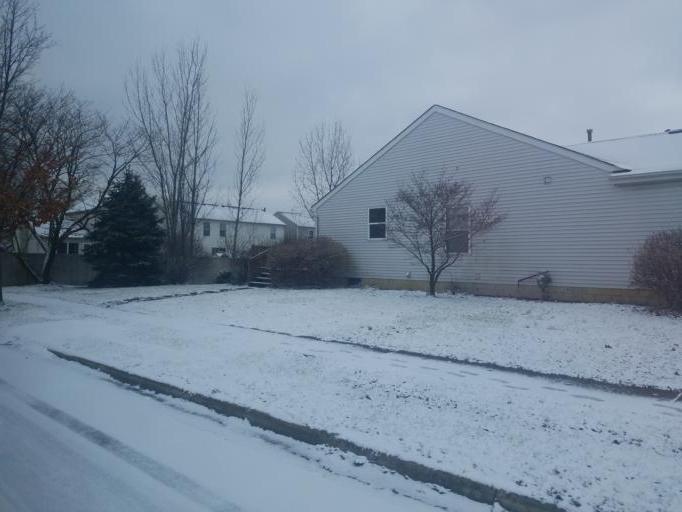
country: US
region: Ohio
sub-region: Franklin County
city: Reynoldsburg
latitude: 39.9960
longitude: -82.7896
